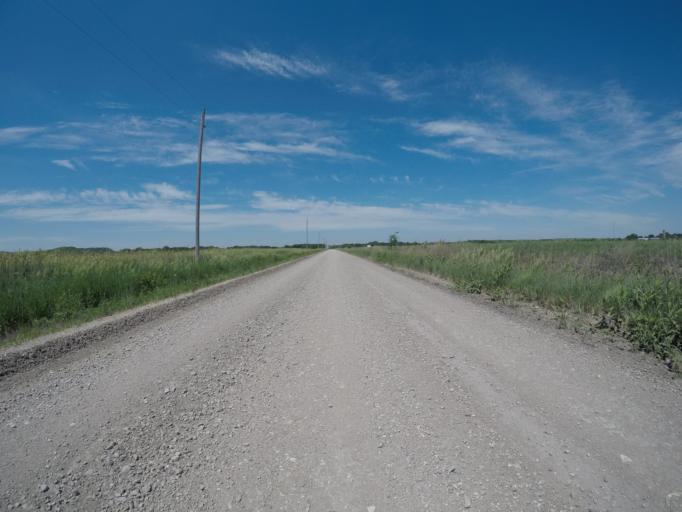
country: US
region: Kansas
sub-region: Wabaunsee County
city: Alma
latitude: 39.0582
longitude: -96.2214
